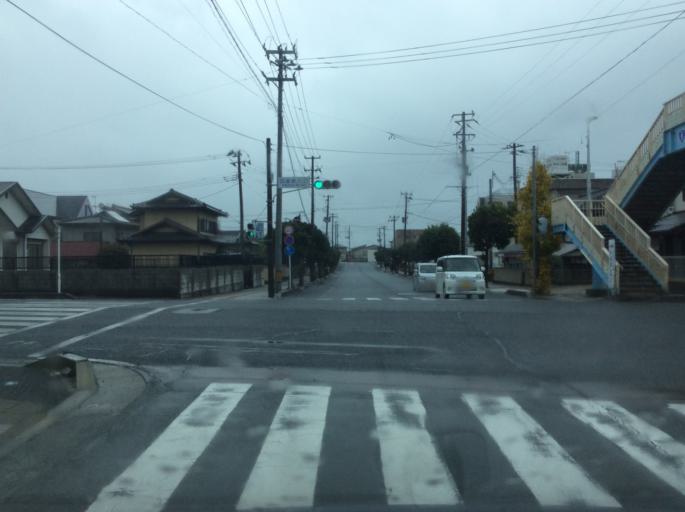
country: JP
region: Fukushima
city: Iwaki
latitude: 37.1011
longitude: 140.9846
